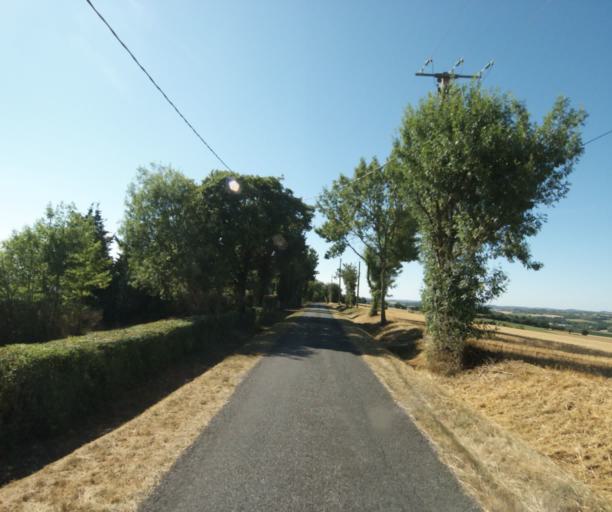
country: FR
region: Midi-Pyrenees
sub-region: Departement de la Haute-Garonne
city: Saint-Felix-Lauragais
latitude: 43.5167
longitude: 1.9206
